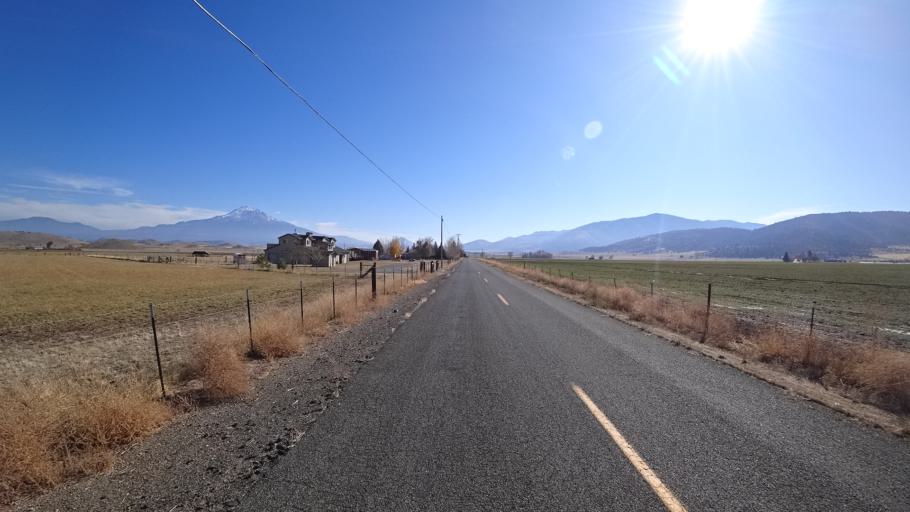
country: US
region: California
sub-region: Siskiyou County
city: Montague
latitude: 41.5446
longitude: -122.5399
